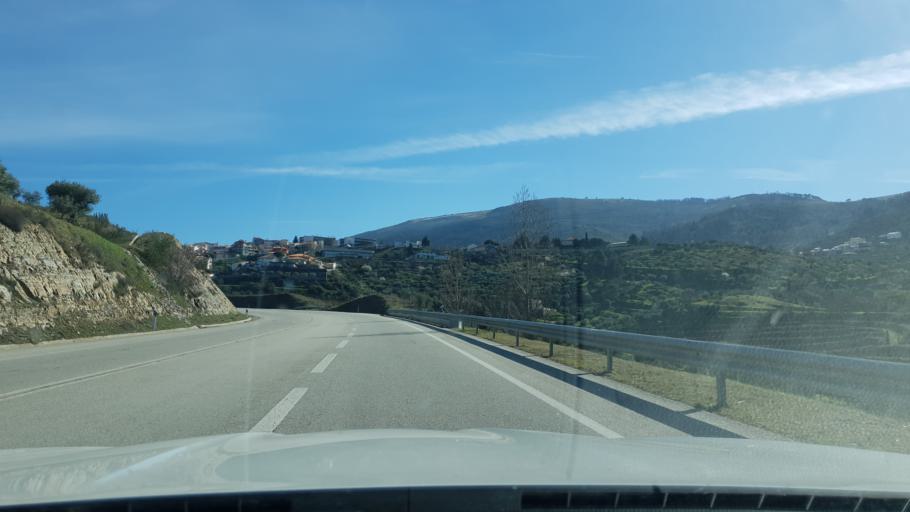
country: PT
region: Braganca
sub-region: Torre de Moncorvo
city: Torre de Moncorvo
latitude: 41.1772
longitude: -7.0665
